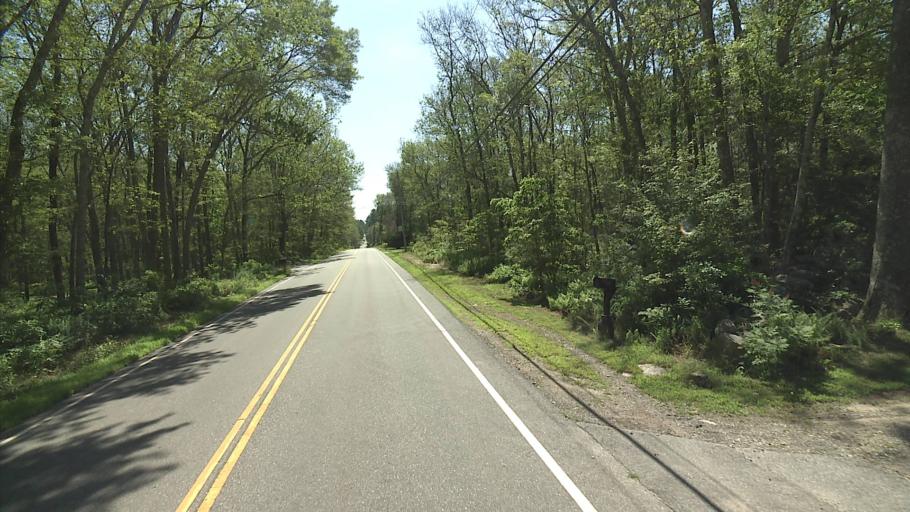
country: US
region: Connecticut
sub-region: Windham County
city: Moosup
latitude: 41.7015
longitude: -71.8044
